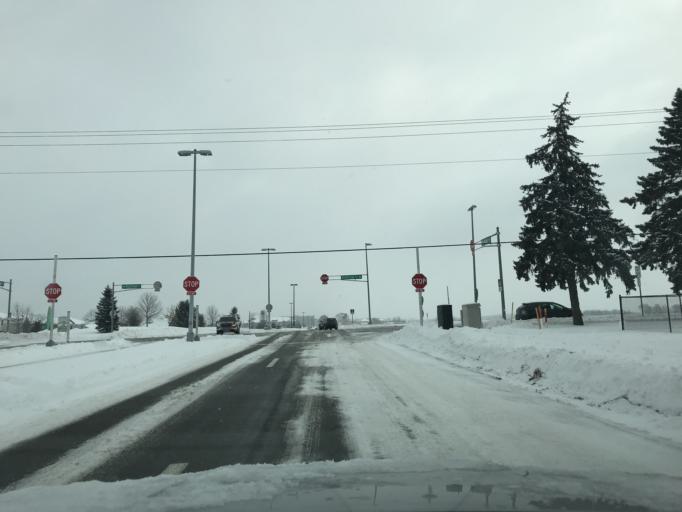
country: US
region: Wisconsin
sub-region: Dane County
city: Sun Prairie
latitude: 43.1648
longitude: -89.2857
